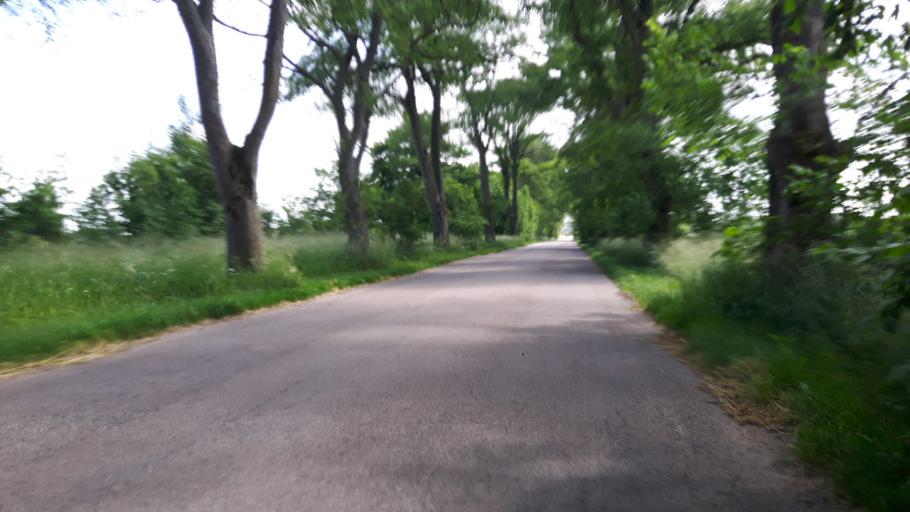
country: PL
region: Pomeranian Voivodeship
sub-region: Powiat wejherowski
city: Choczewo
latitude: 54.7393
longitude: 17.8188
